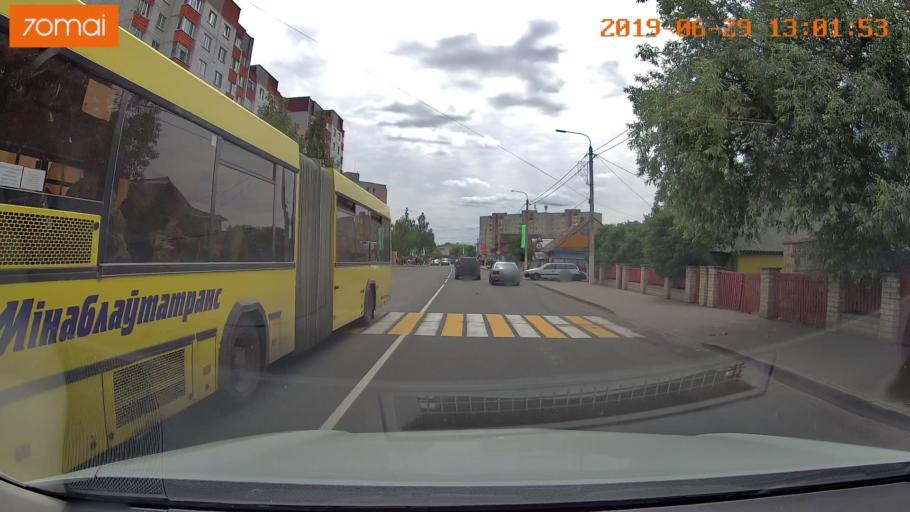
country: BY
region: Minsk
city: Slutsk
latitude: 53.0364
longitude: 27.5597
